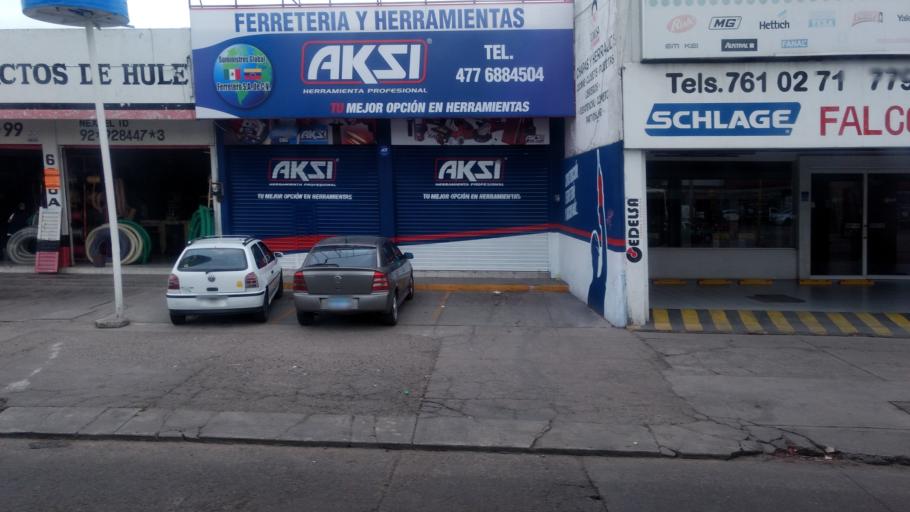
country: MX
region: Guanajuato
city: Leon
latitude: 21.1381
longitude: -101.6759
